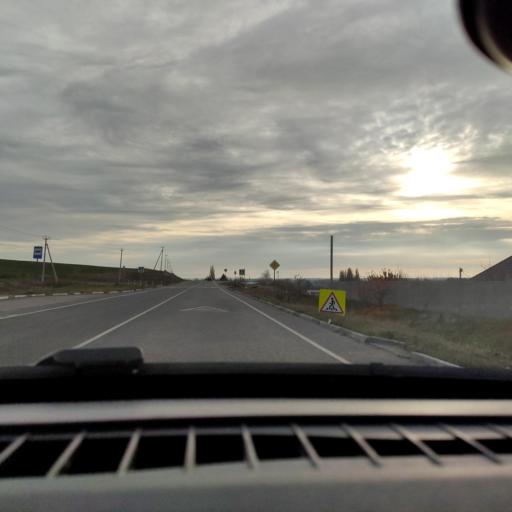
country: RU
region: Belgorod
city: Alekseyevka
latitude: 50.6438
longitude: 38.6454
